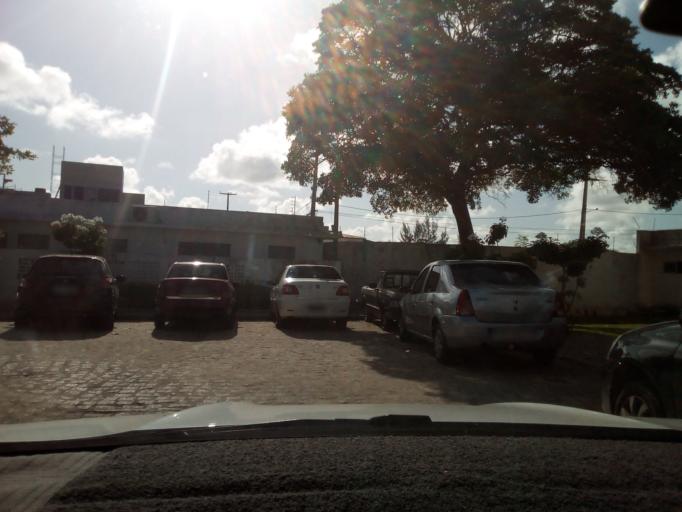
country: BR
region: Paraiba
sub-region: Cabedelo
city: Cabedelo
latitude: -7.0447
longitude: -34.8484
